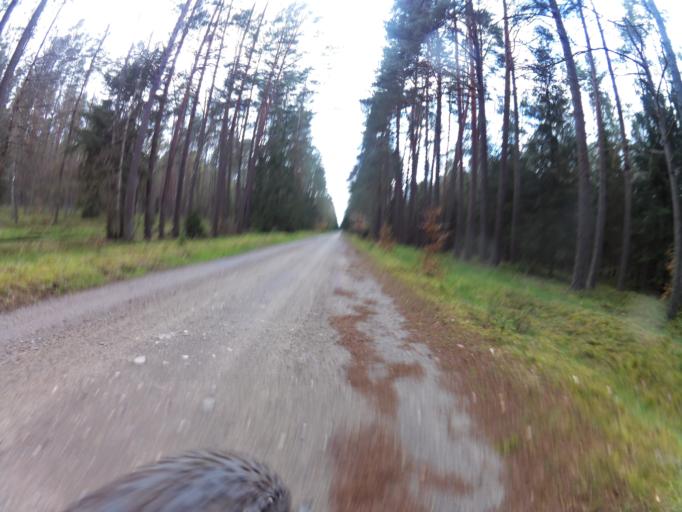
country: PL
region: West Pomeranian Voivodeship
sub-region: Powiat slawienski
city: Slawno
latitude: 54.3182
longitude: 16.7909
